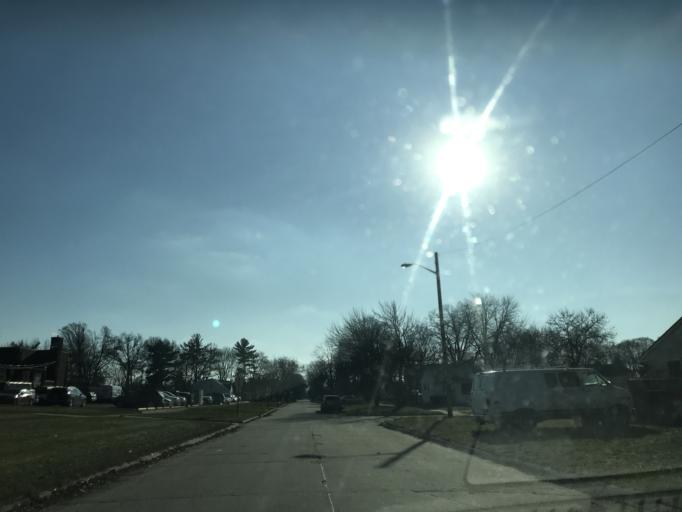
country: US
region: Michigan
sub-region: Oakland County
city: Madison Heights
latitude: 42.4942
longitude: -83.1150
